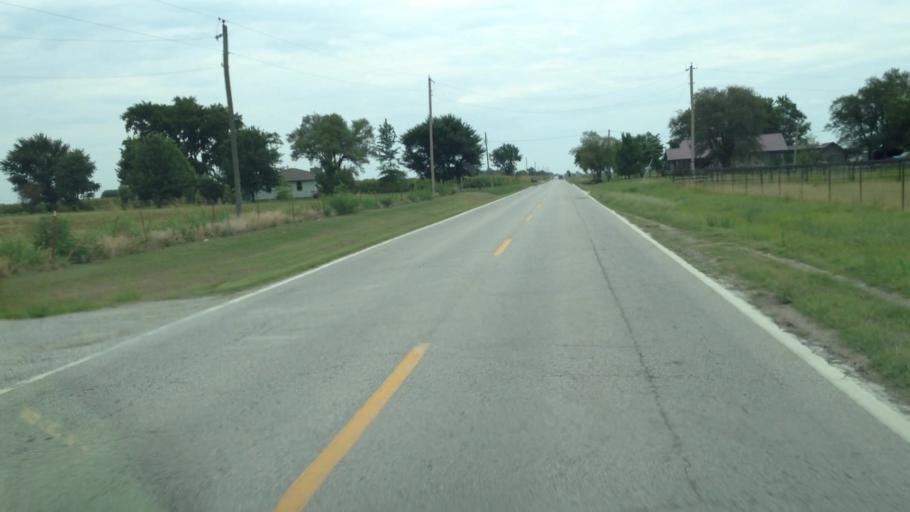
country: US
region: Oklahoma
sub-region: Delaware County
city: Cleora
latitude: 36.6184
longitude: -94.9815
